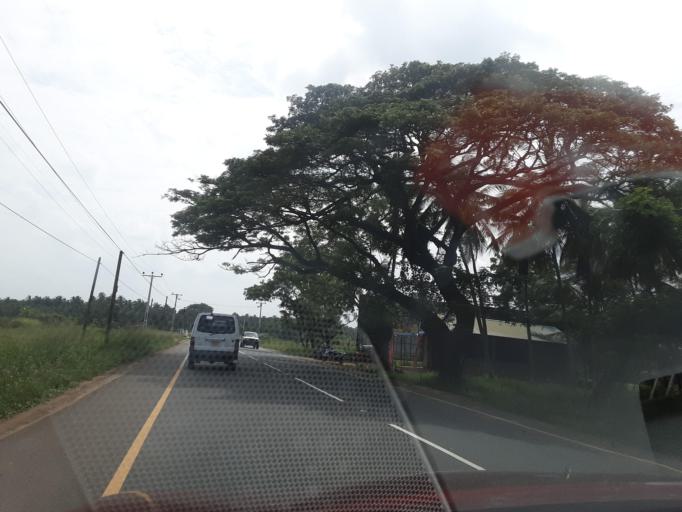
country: LK
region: North Central
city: Anuradhapura
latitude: 8.4760
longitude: 80.5128
